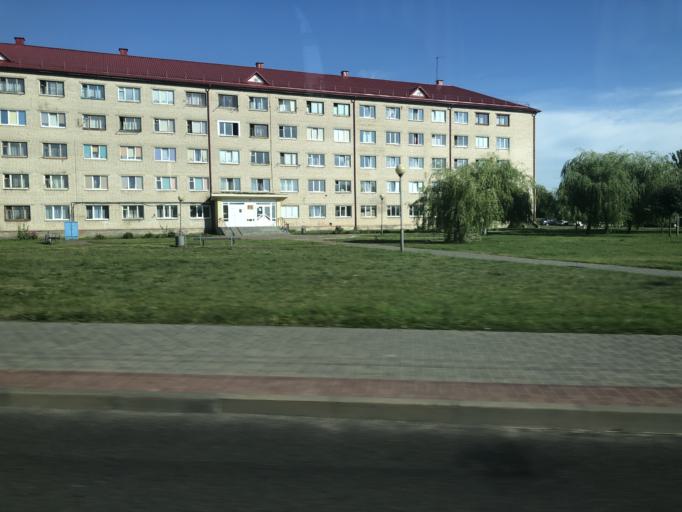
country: BY
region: Grodnenskaya
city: Hrodna
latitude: 53.6535
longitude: 23.7946
